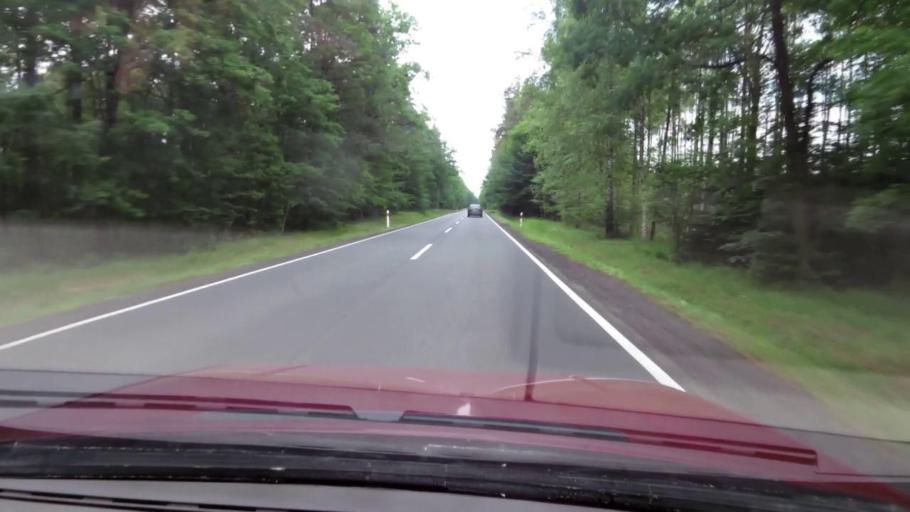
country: PL
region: Pomeranian Voivodeship
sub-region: Powiat bytowski
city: Trzebielino
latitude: 54.2223
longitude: 17.0877
